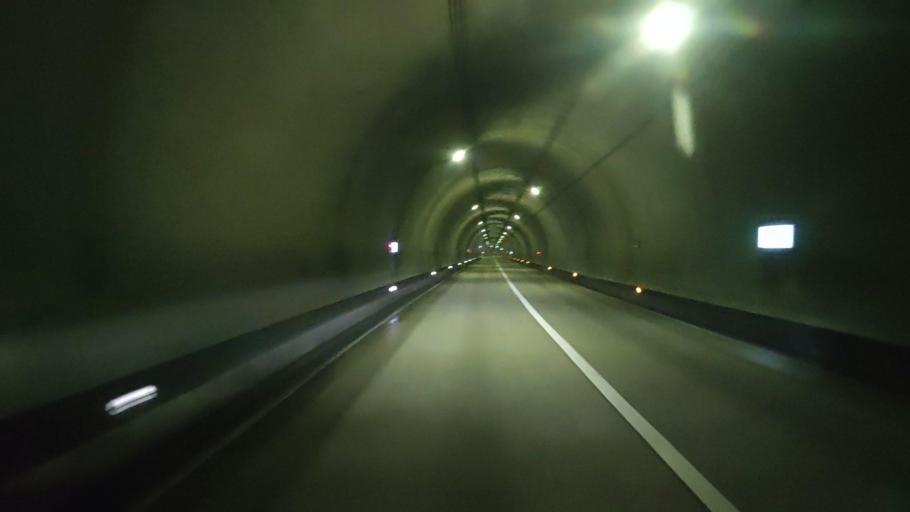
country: JP
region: Wakayama
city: Shingu
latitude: 33.8541
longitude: 135.8540
